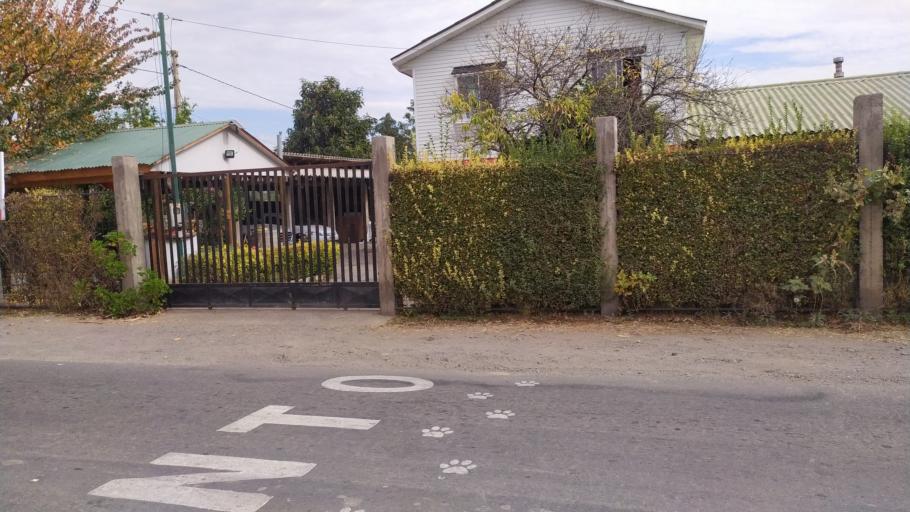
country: CL
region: Valparaiso
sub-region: Provincia de San Felipe
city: Llaillay
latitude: -32.7828
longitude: -70.9129
